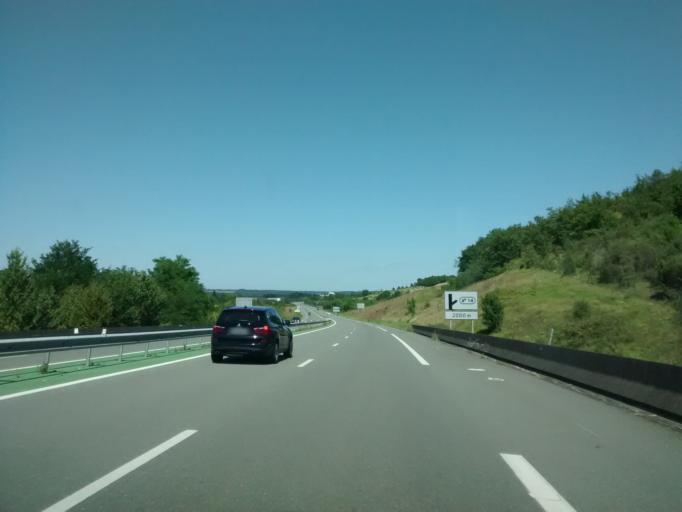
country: FR
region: Aquitaine
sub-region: Departement de la Dordogne
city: Saint-Astier
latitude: 45.1268
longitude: 0.5313
